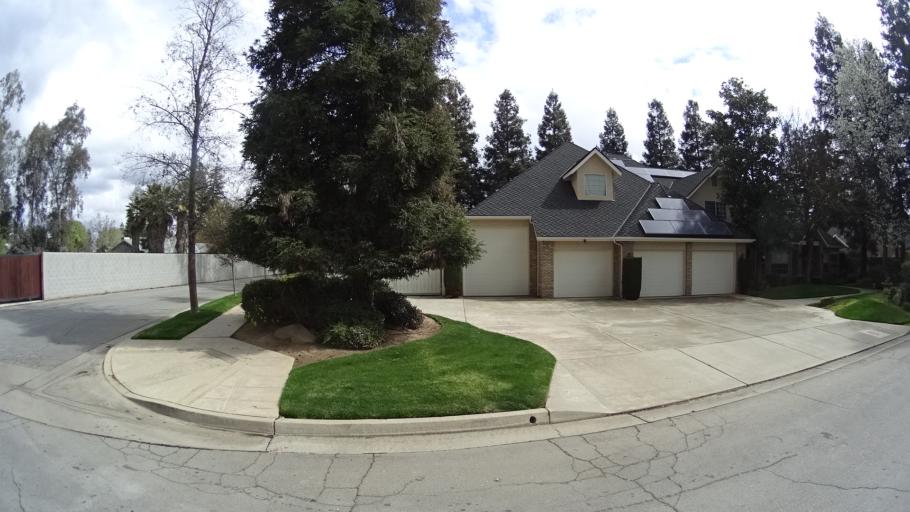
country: US
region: California
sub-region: Fresno County
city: Fresno
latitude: 36.8330
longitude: -119.8292
